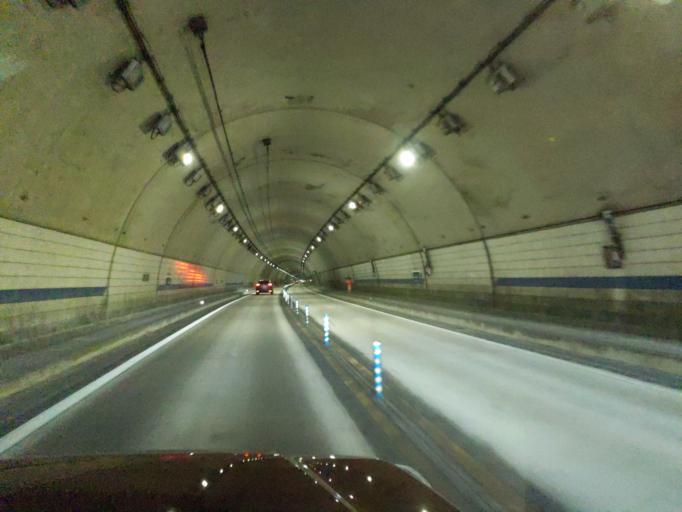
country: JP
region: Tokushima
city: Anan
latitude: 33.7574
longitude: 134.5594
